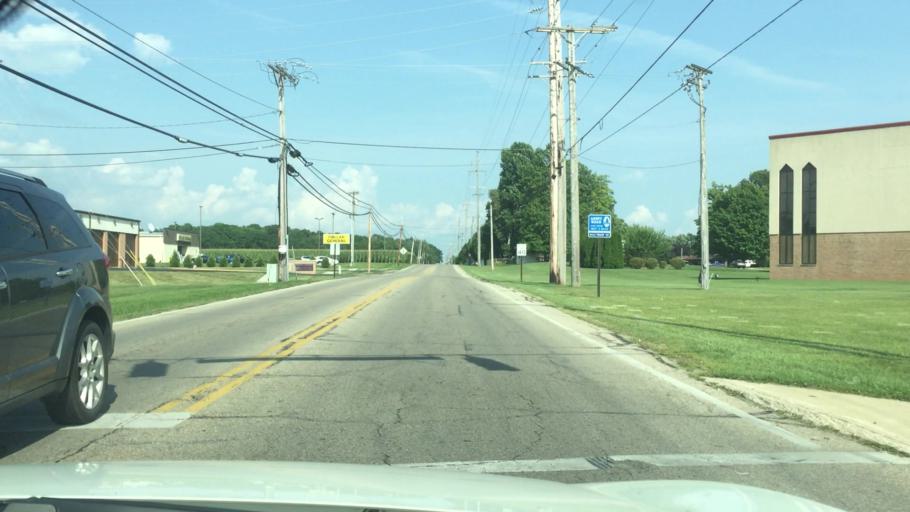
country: US
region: Ohio
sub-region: Clark County
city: Northridge
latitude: 39.9953
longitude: -83.7708
